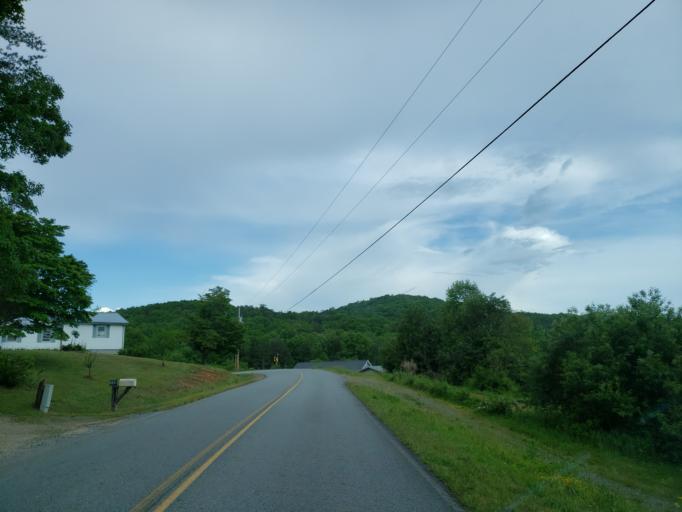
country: US
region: Georgia
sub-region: Fannin County
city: Blue Ridge
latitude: 34.8675
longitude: -84.3654
